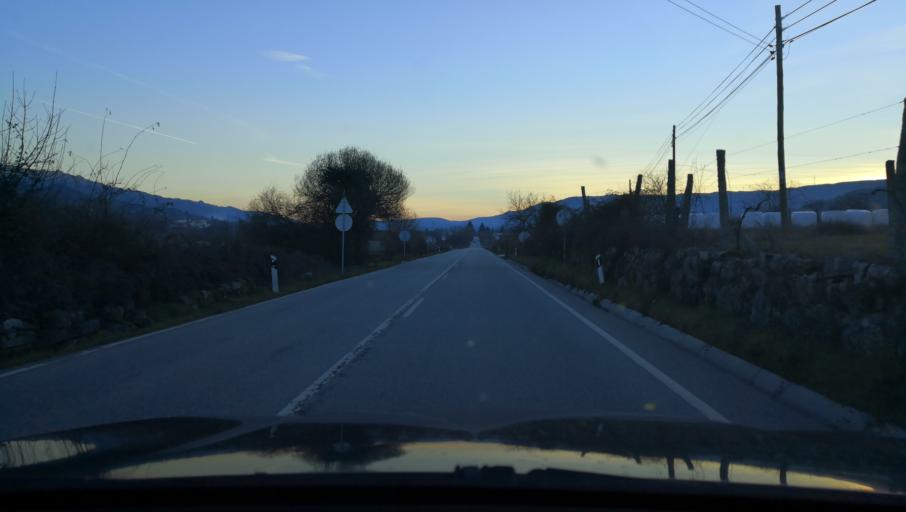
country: PT
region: Vila Real
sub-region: Vila Pouca de Aguiar
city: Vila Pouca de Aguiar
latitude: 41.4797
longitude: -7.6557
